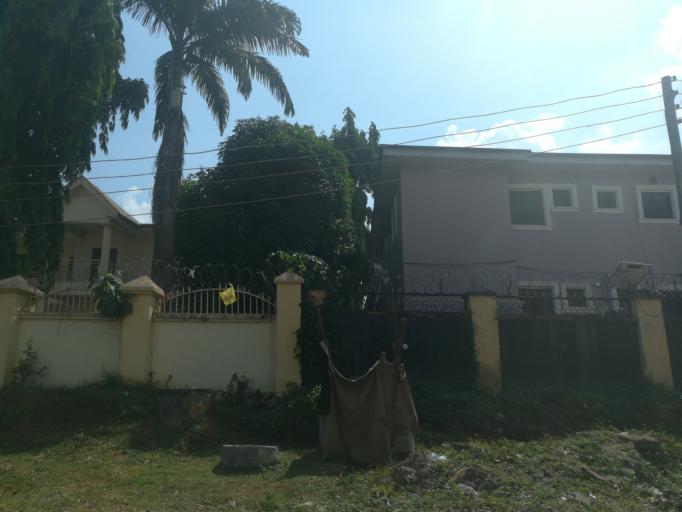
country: NG
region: Abuja Federal Capital Territory
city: Abuja
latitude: 9.0537
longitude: 7.4480
